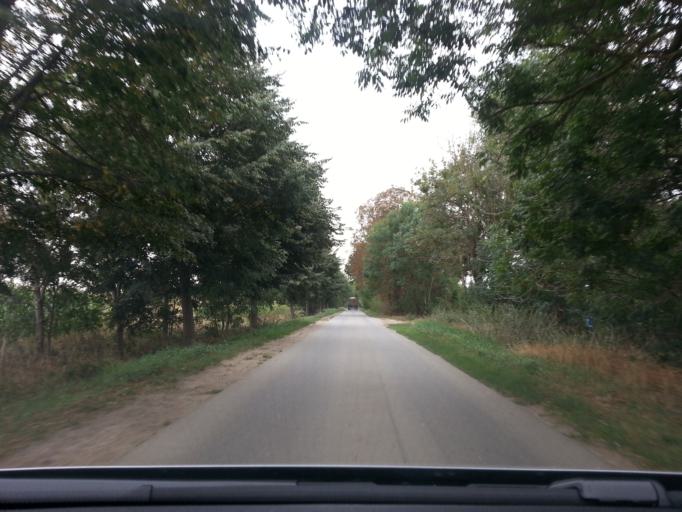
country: DE
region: Mecklenburg-Vorpommern
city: Ferdinandshof
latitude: 53.6635
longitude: 13.9174
